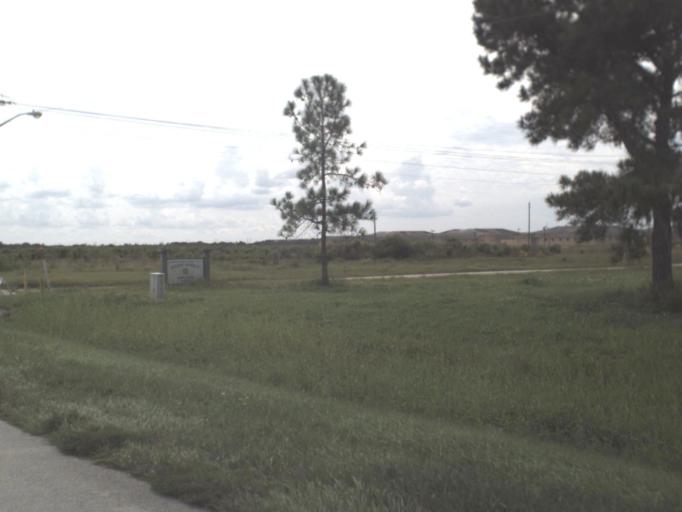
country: US
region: Florida
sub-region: DeSoto County
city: Southeast Arcadia
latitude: 27.1331
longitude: -81.7962
